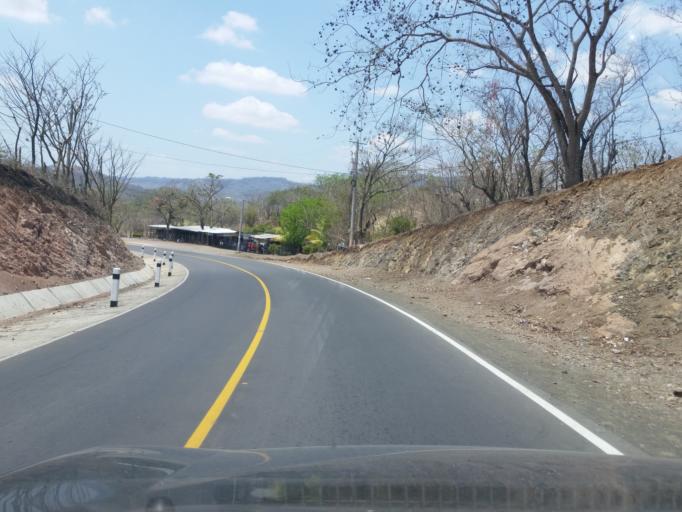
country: NI
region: Boaco
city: Boaco
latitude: 12.4903
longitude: -85.6375
